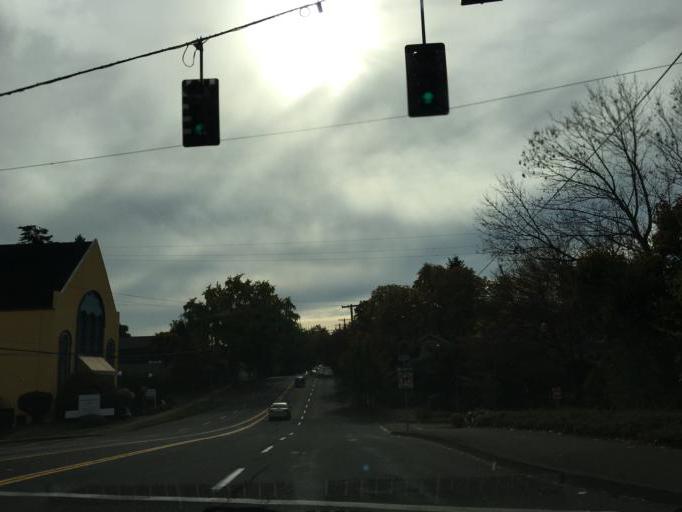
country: US
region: Oregon
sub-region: Multnomah County
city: Portland
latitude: 45.5329
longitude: -122.6230
